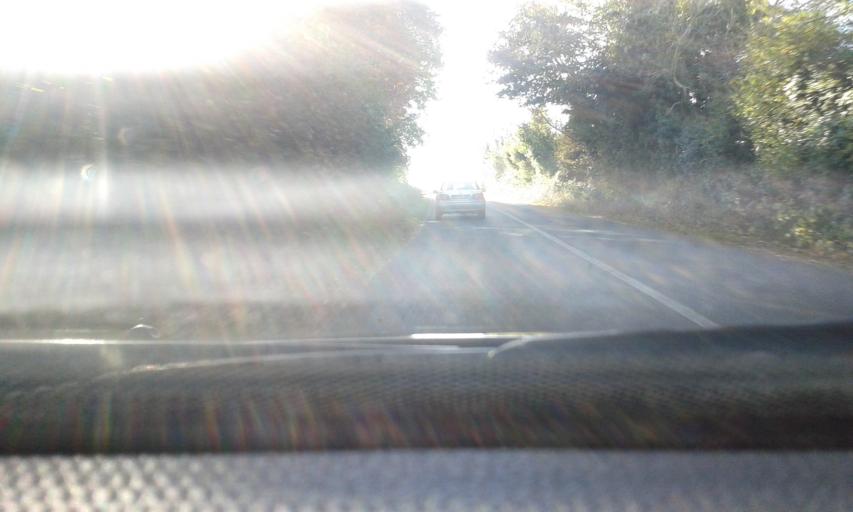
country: IE
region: Leinster
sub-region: Kildare
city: Rathangan
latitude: 53.2137
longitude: -6.9992
